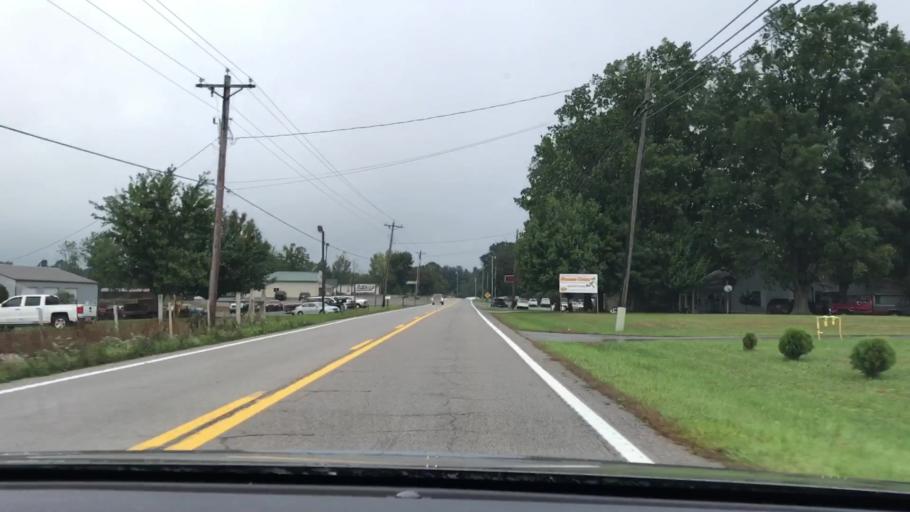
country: US
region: Tennessee
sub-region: Fentress County
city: Grimsley
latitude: 36.2305
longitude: -85.0087
